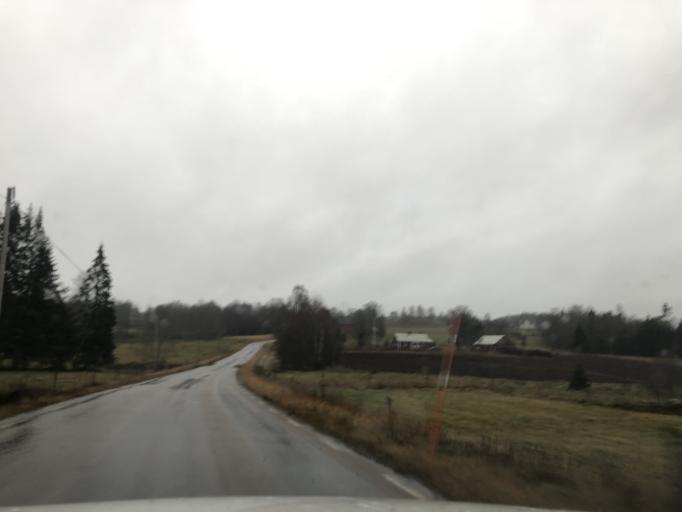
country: SE
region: Vaestra Goetaland
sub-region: Ulricehamns Kommun
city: Ulricehamn
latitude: 57.8543
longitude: 13.5483
